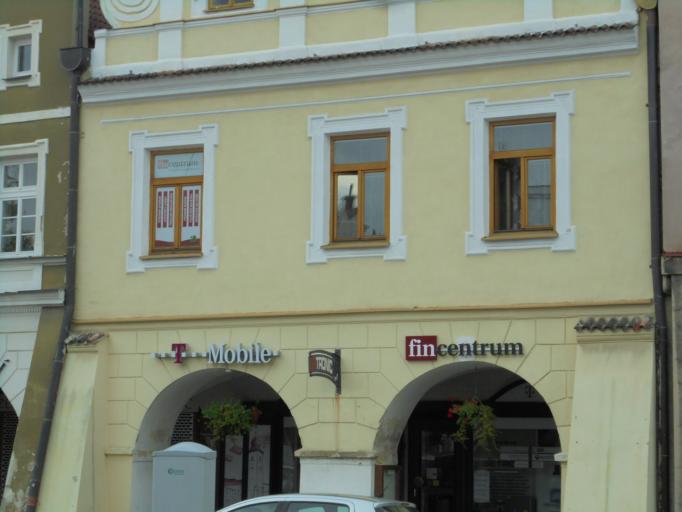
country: CZ
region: Pardubicky
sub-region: Okres Svitavy
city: Svitavy
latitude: 49.7552
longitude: 16.4692
